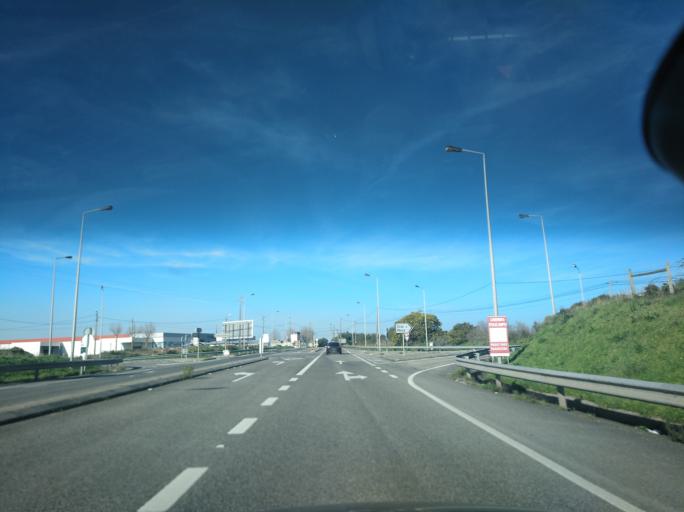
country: PT
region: Lisbon
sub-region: Sintra
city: Pero Pinheiro
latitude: 38.8724
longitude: -9.3297
